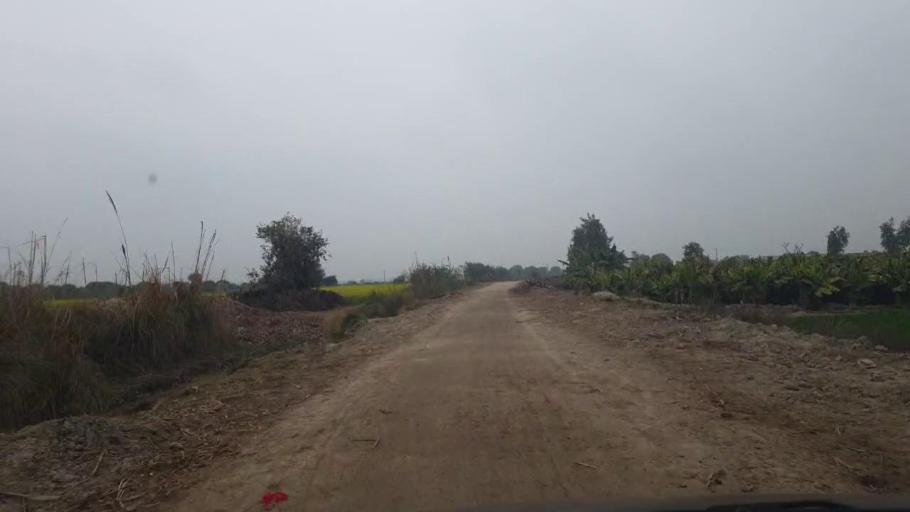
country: PK
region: Sindh
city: Tando Adam
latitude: 25.8488
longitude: 68.6762
